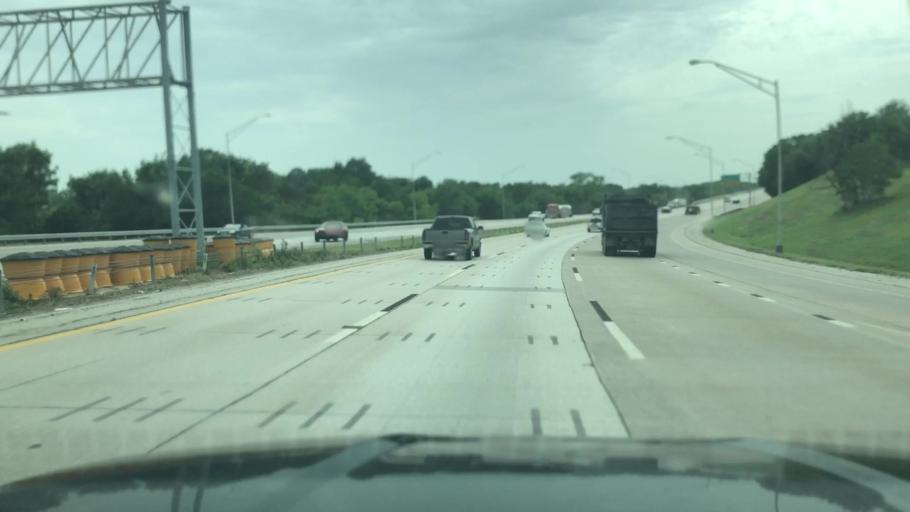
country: US
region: Oklahoma
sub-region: Tulsa County
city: Tulsa
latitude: 36.1565
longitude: -96.0230
